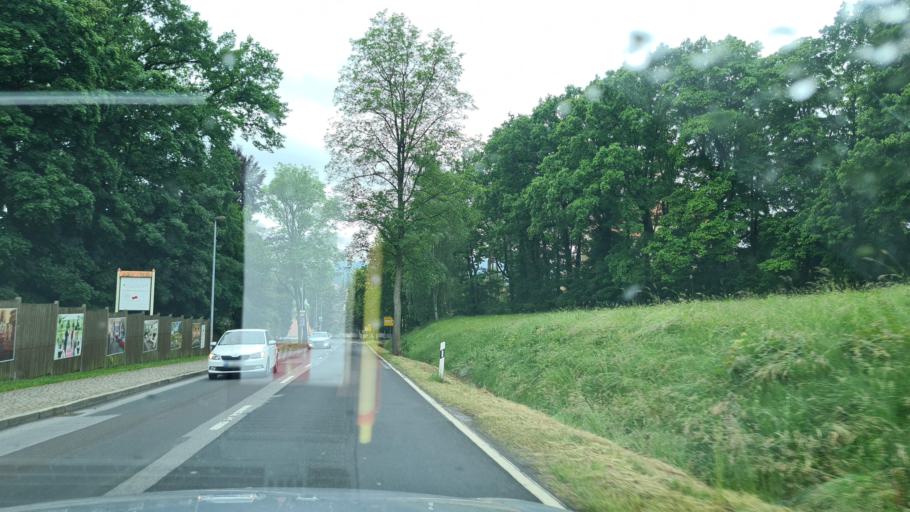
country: DE
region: Saxony
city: Kirschau
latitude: 51.0961
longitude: 14.4284
